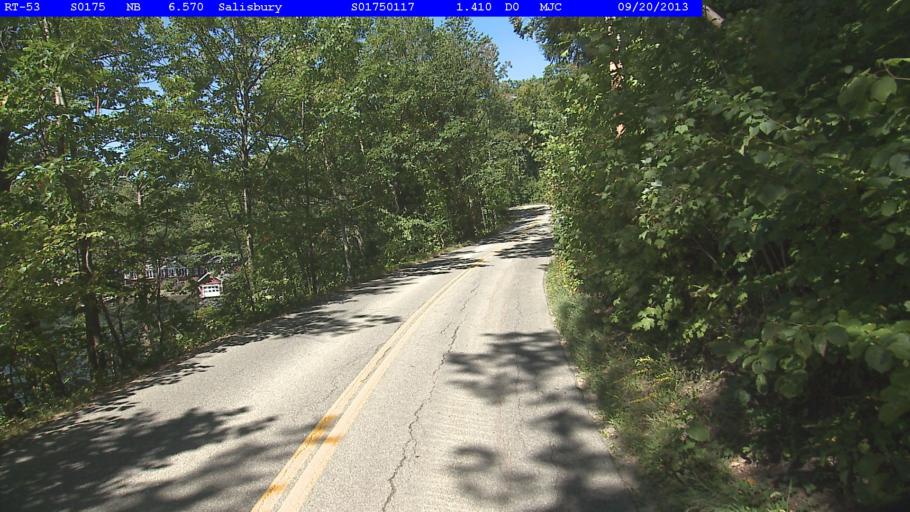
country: US
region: Vermont
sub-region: Rutland County
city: Brandon
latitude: 43.9174
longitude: -73.0690
